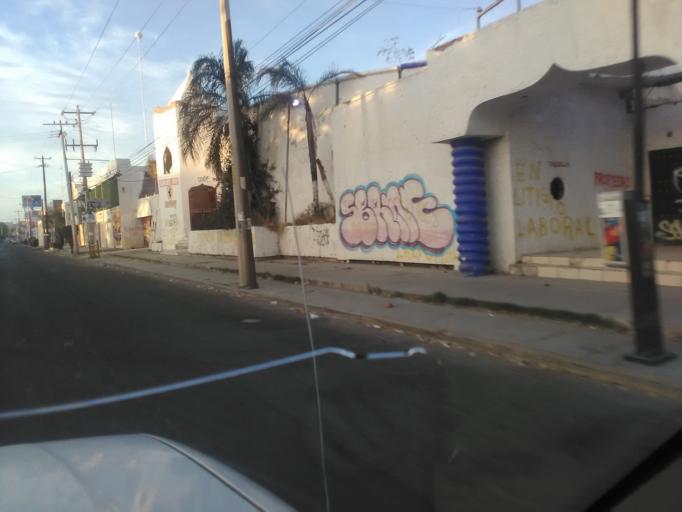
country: MX
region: Durango
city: Victoria de Durango
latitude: 24.0027
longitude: -104.6625
